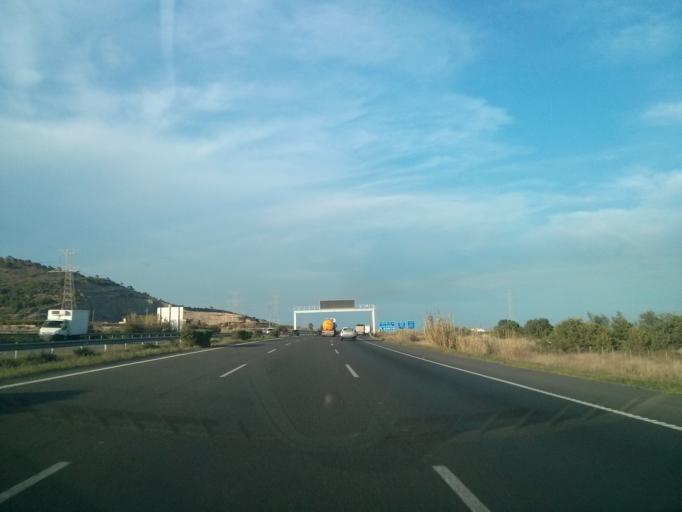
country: ES
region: Valencia
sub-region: Provincia de Valencia
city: Sagunto
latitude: 39.6940
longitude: -0.2815
